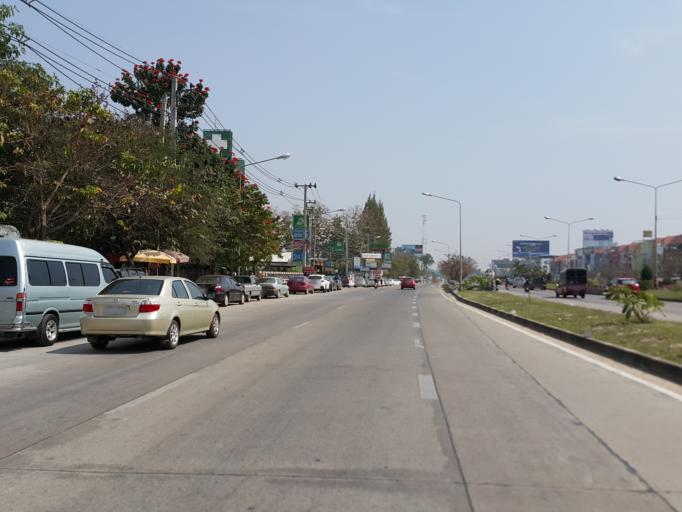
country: TH
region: Chiang Mai
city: Chiang Mai
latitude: 18.8122
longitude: 98.9899
